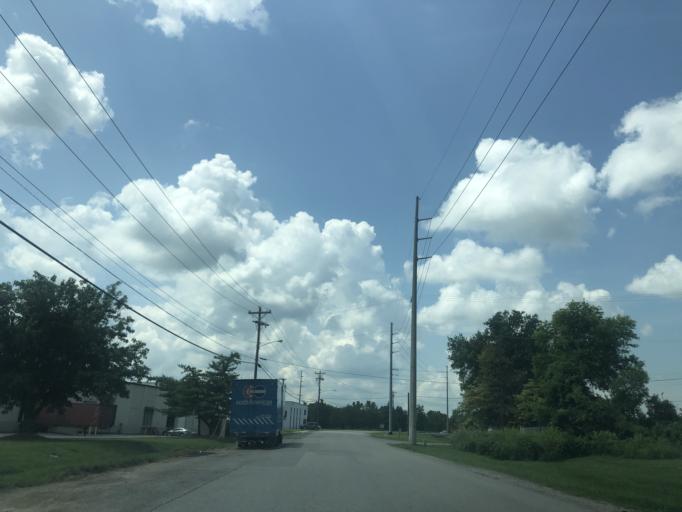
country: US
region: Tennessee
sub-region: Rutherford County
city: La Vergne
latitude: 36.0141
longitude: -86.6012
